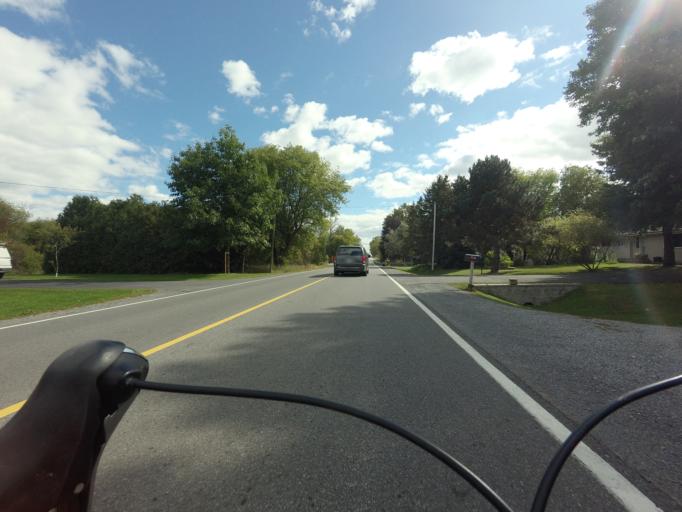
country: CA
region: Ontario
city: Bells Corners
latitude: 45.2058
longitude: -75.7005
